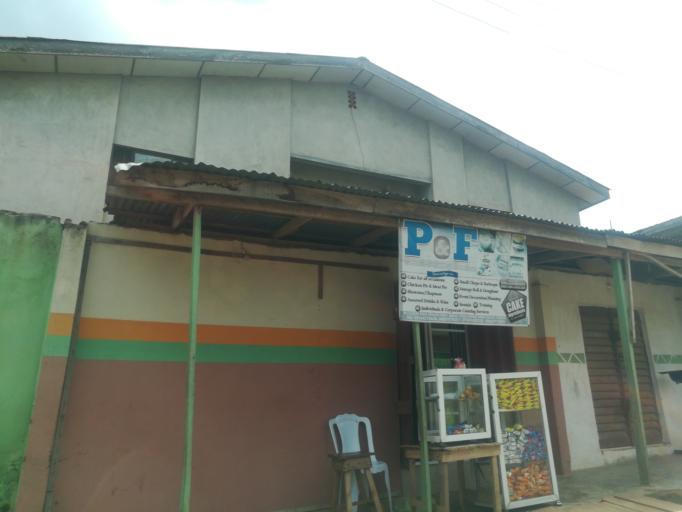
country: NG
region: Oyo
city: Ibadan
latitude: 7.4376
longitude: 3.9406
